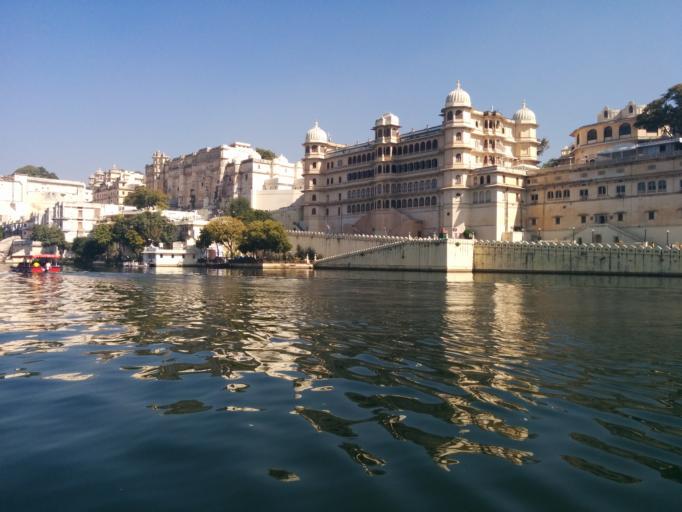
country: IN
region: Rajasthan
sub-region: Udaipur
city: Udaipur
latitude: 24.5740
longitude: 73.6823
